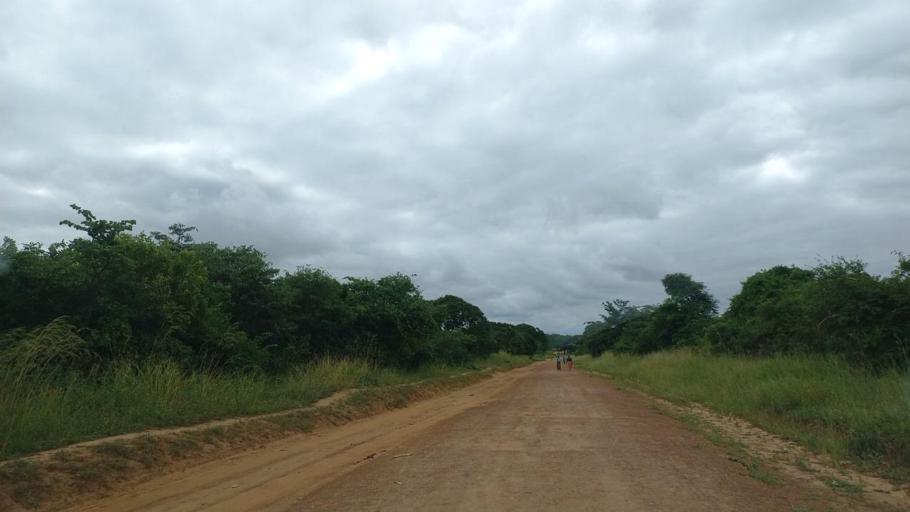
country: ZM
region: Lusaka
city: Chongwe
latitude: -15.4558
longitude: 28.8588
